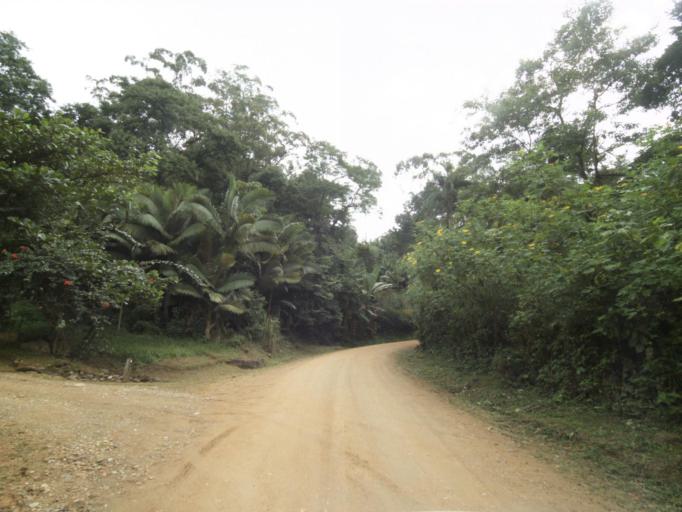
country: BR
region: Santa Catarina
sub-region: Pomerode
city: Pomerode
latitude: -26.7330
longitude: -49.1948
